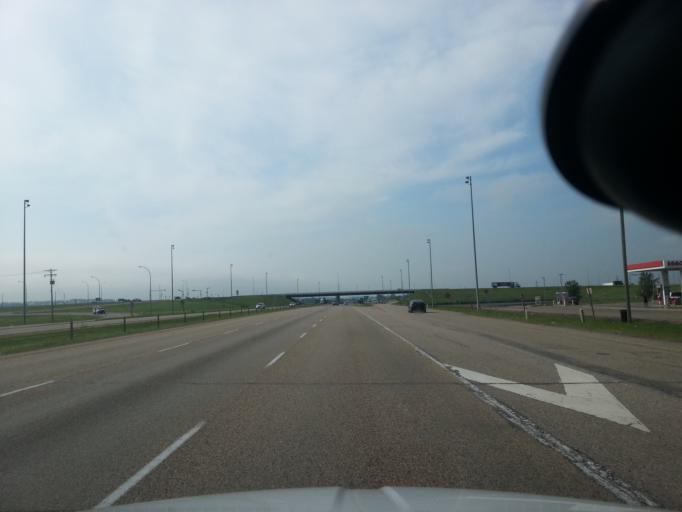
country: CA
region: Alberta
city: Red Deer
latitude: 52.2051
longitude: -113.8142
